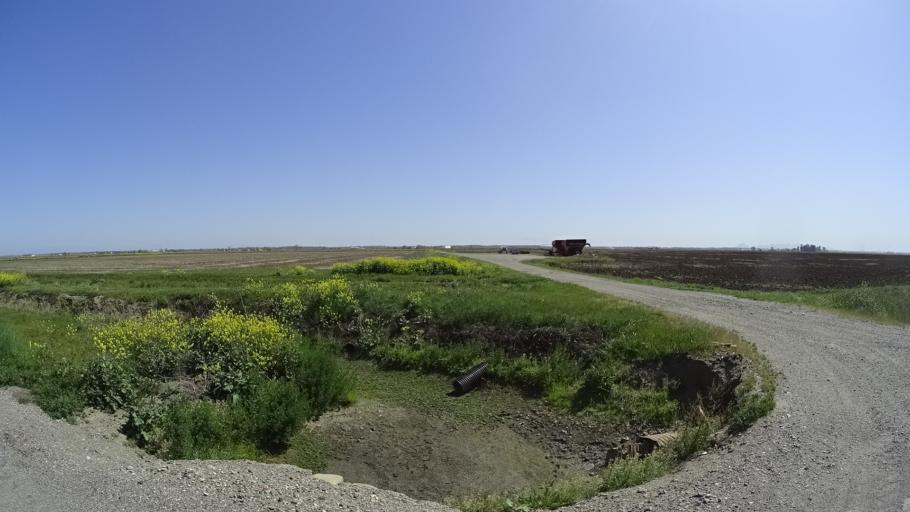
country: US
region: California
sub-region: Glenn County
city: Willows
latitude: 39.4360
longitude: -122.0647
